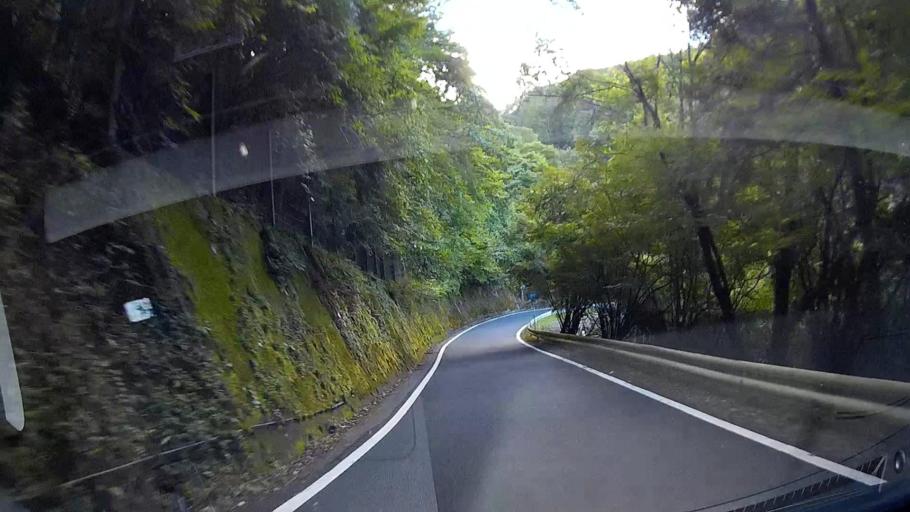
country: JP
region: Shizuoka
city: Shizuoka-shi
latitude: 35.1363
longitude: 138.2728
